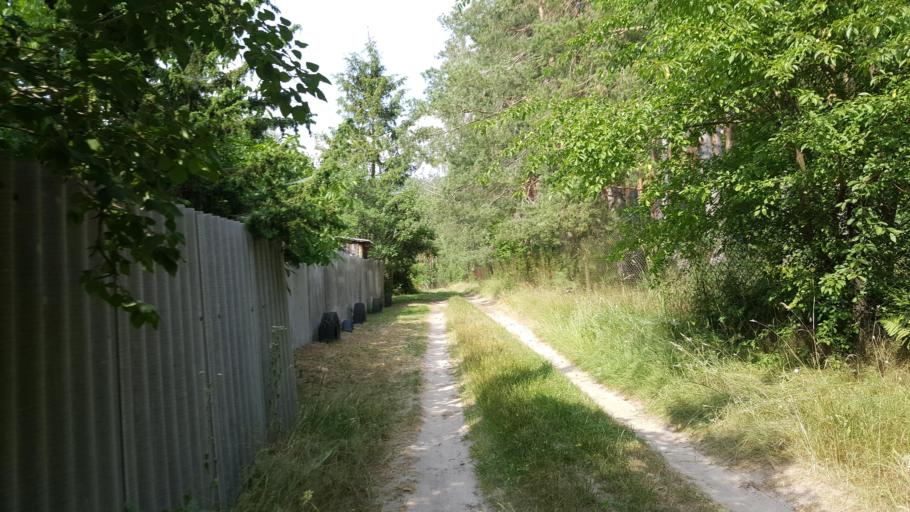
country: BY
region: Brest
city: Kamyanyets
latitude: 52.3665
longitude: 23.8084
